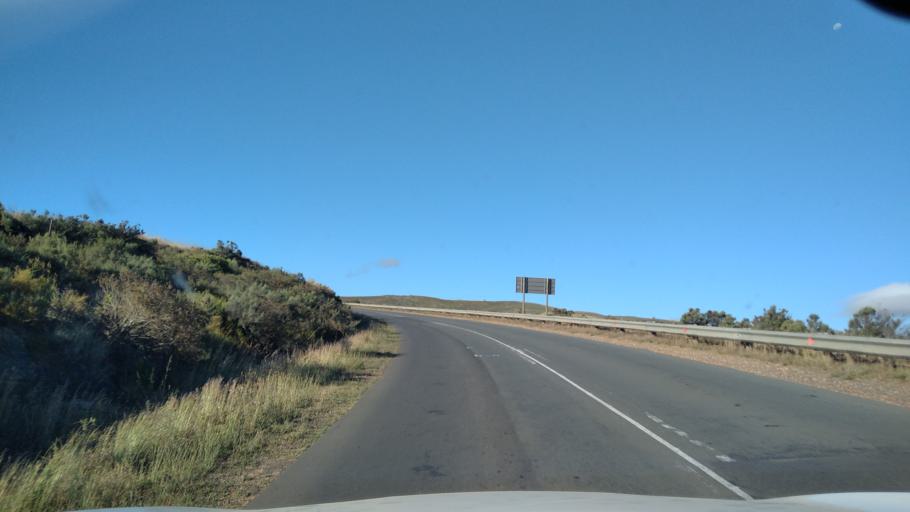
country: ZA
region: Western Cape
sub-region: Overberg District Municipality
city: Caledon
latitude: -34.1584
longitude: 19.3053
